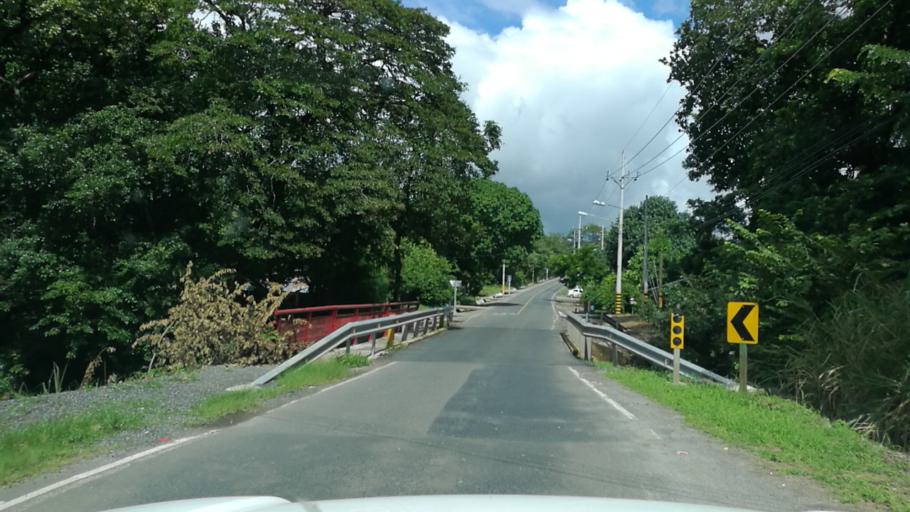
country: CR
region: Guanacaste
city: Bagaces
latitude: 10.5360
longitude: -85.2552
